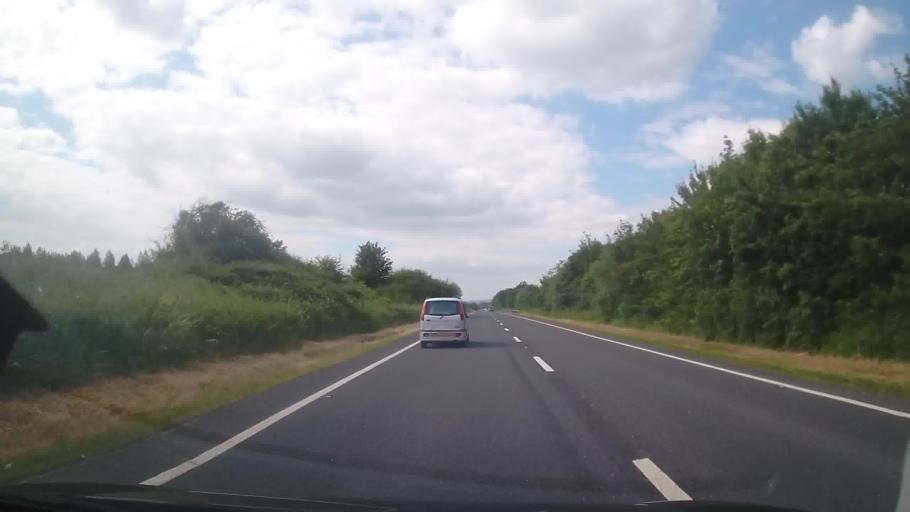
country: GB
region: England
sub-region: Herefordshire
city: Hope under Dinmore
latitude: 52.2061
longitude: -2.7216
